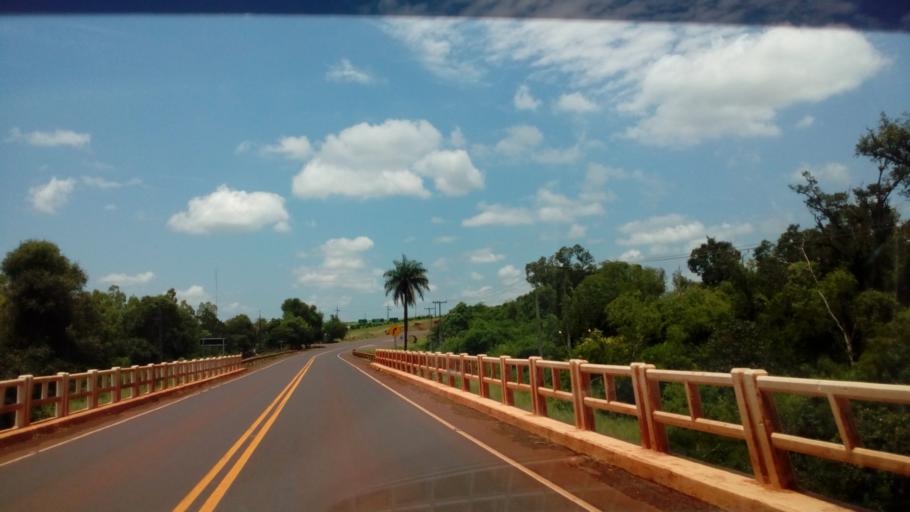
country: PY
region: Alto Parana
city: Naranjal
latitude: -26.0472
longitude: -55.1296
